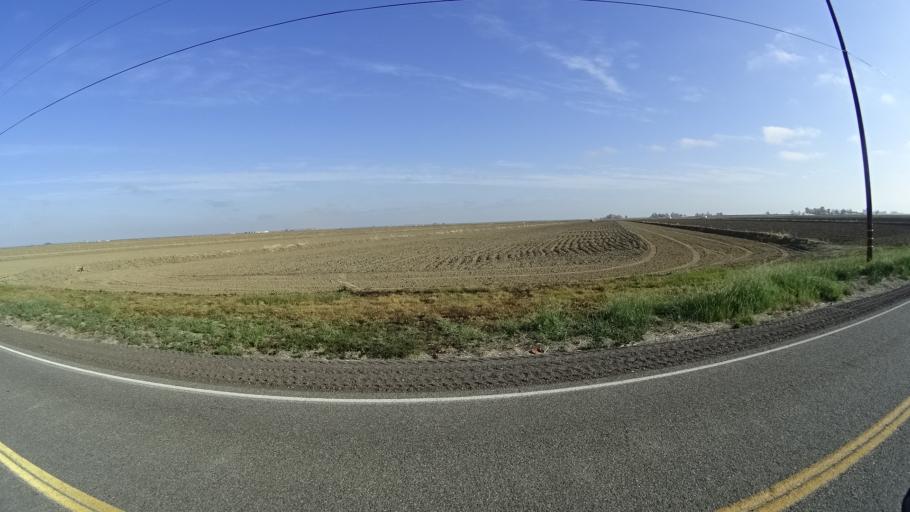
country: US
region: California
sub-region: Glenn County
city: Willows
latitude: 39.5820
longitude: -122.1031
